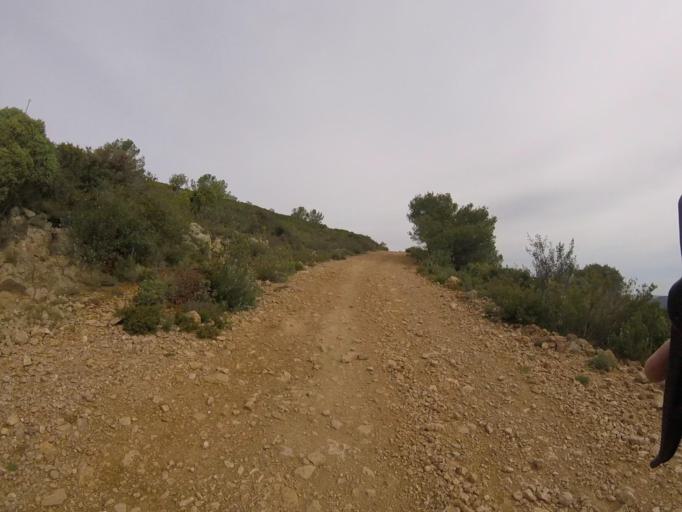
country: ES
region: Valencia
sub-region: Provincia de Castello
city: Benicassim
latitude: 40.0859
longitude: 0.0382
